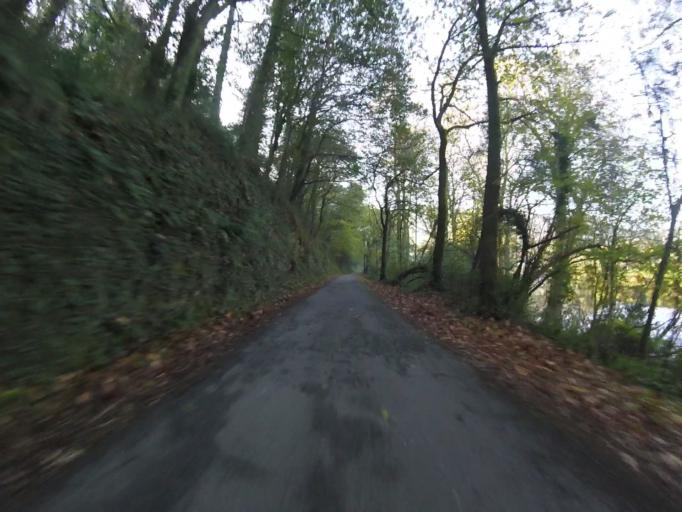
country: ES
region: Basque Country
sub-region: Provincia de Guipuzcoa
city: Usurbil
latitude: 43.2720
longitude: -2.0650
